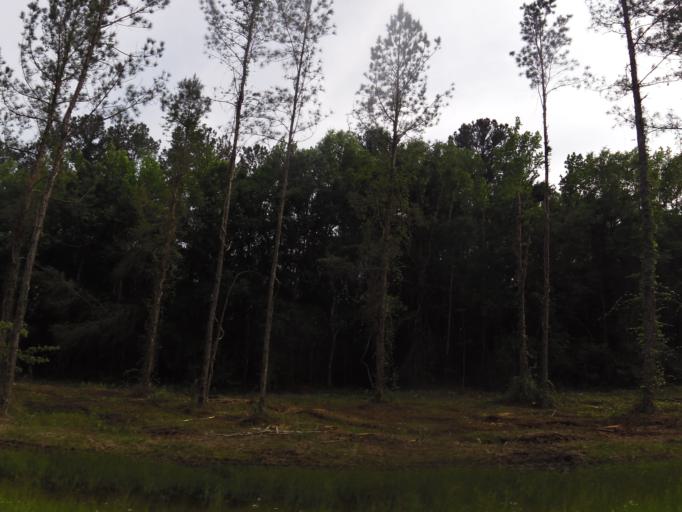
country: US
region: Georgia
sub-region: Camden County
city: Kingsland
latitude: 30.6989
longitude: -81.7731
